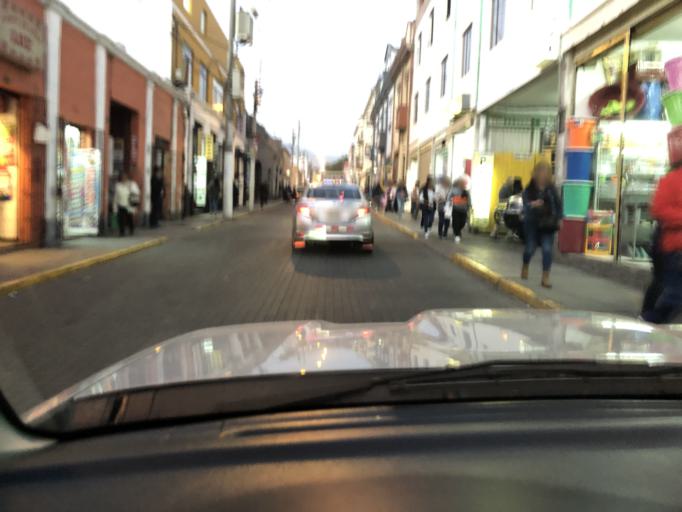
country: PE
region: Arequipa
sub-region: Provincia de Arequipa
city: Arequipa
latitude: -16.4018
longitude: -71.5326
